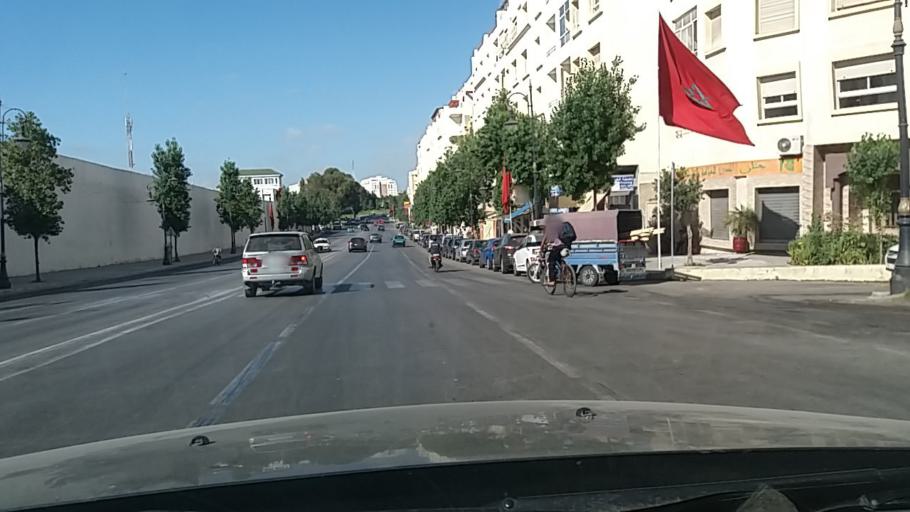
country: MA
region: Tanger-Tetouan
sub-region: Tanger-Assilah
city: Tangier
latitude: 35.7607
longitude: -5.8411
